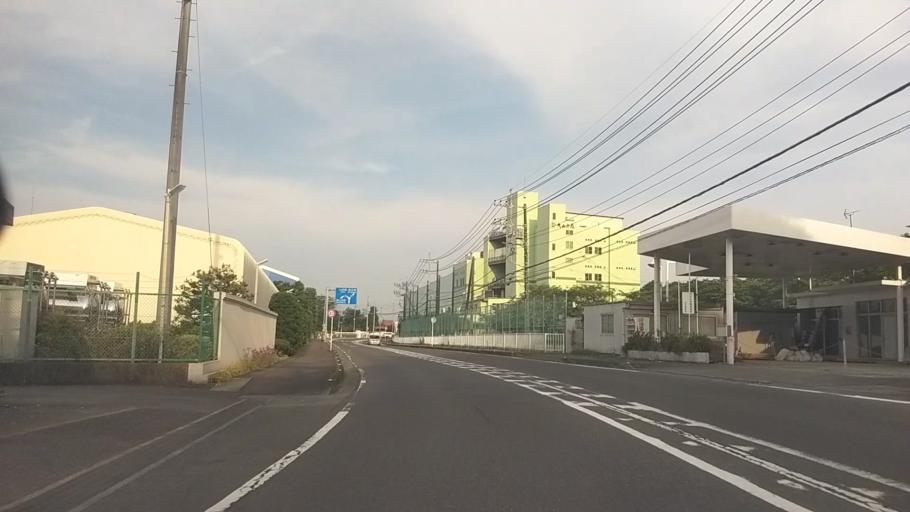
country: JP
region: Kanagawa
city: Odawara
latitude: 35.3483
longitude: 139.0945
